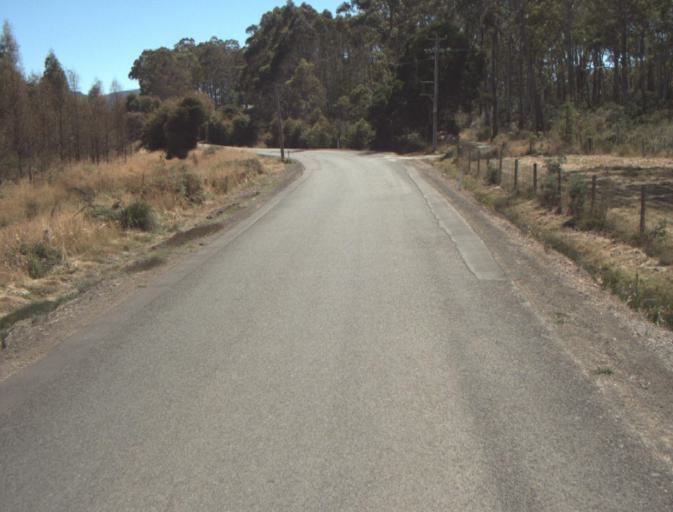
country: AU
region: Tasmania
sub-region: Launceston
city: Newstead
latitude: -41.3831
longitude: 147.2974
